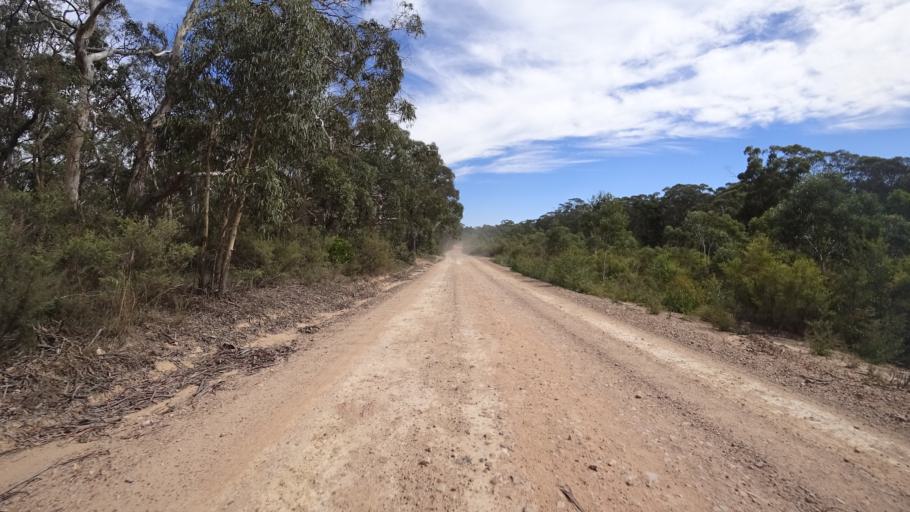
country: AU
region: New South Wales
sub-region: Lithgow
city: Lithgow
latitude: -33.3433
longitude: 150.2540
